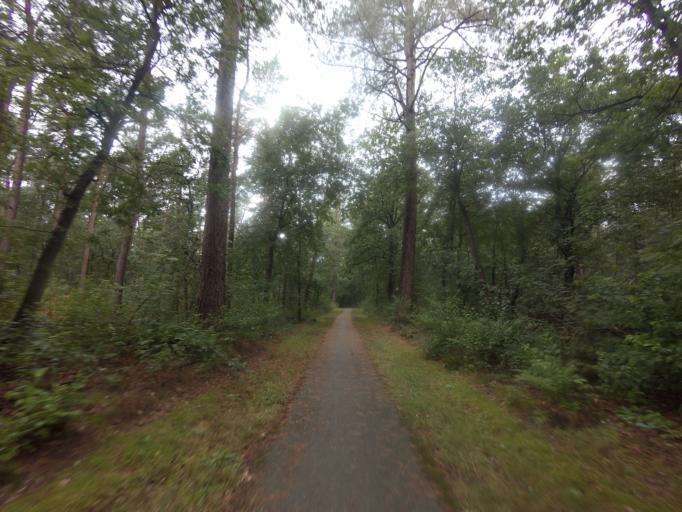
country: NL
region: Overijssel
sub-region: Gemeente Staphorst
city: Staphorst
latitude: 52.6194
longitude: 6.3098
